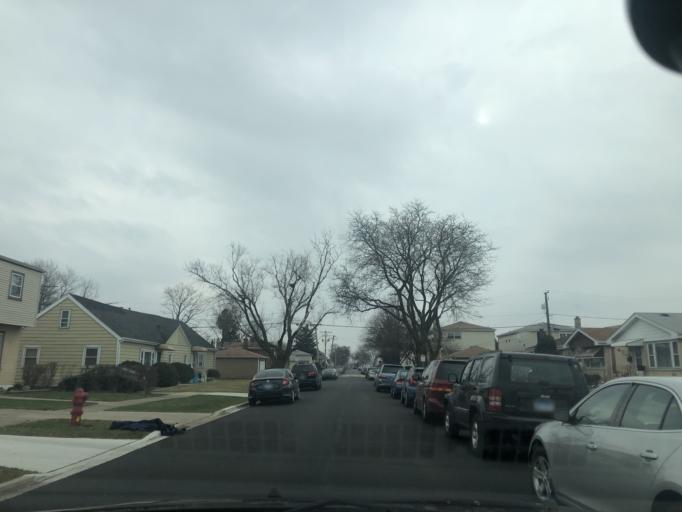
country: US
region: Illinois
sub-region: Cook County
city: Schiller Park
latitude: 41.9707
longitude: -87.8674
